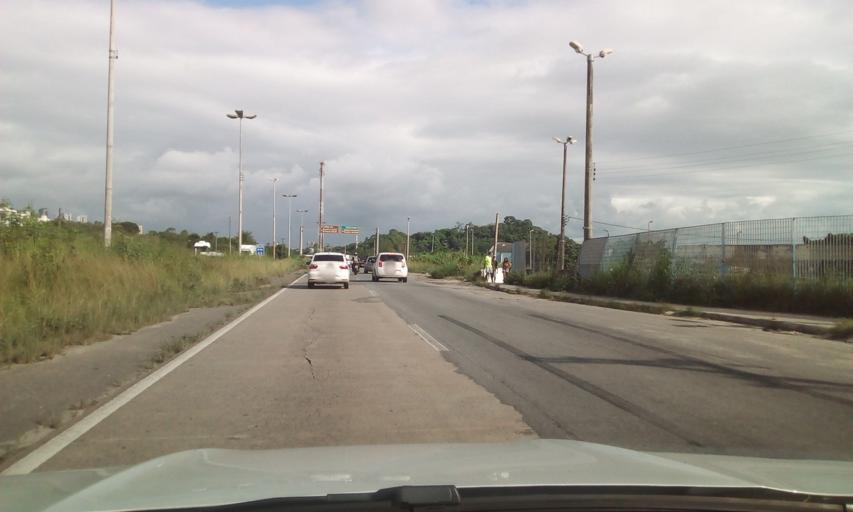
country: BR
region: Pernambuco
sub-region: Recife
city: Recife
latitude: -8.0081
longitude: -34.9378
